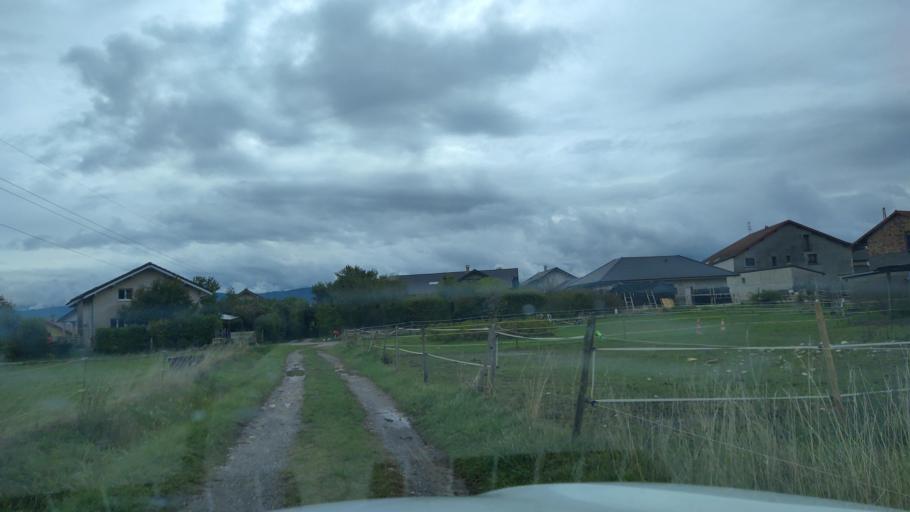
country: FR
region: Rhone-Alpes
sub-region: Departement de la Savoie
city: Les Marches
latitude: 45.5086
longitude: 5.9995
